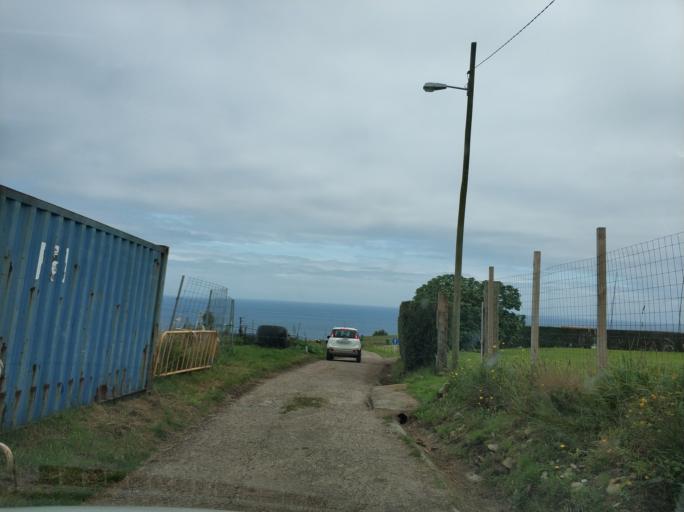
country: ES
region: Asturias
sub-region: Province of Asturias
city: Cudillero
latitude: 43.5631
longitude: -6.2979
